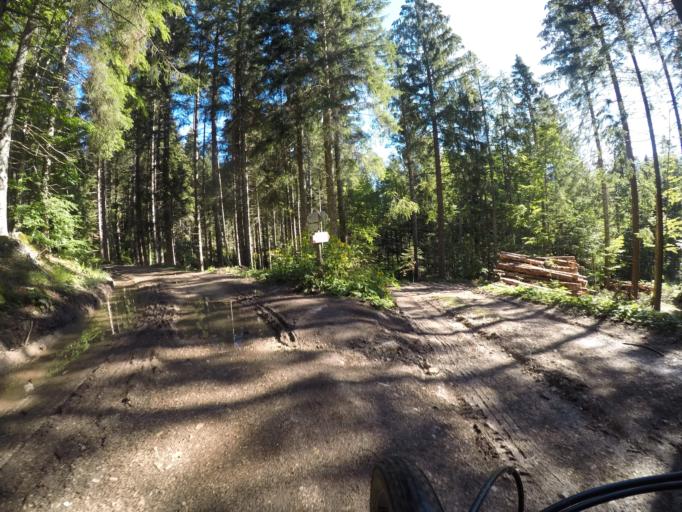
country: IT
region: Veneto
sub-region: Provincia di Vicenza
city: Canove di Roana
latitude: 45.8995
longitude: 11.4828
